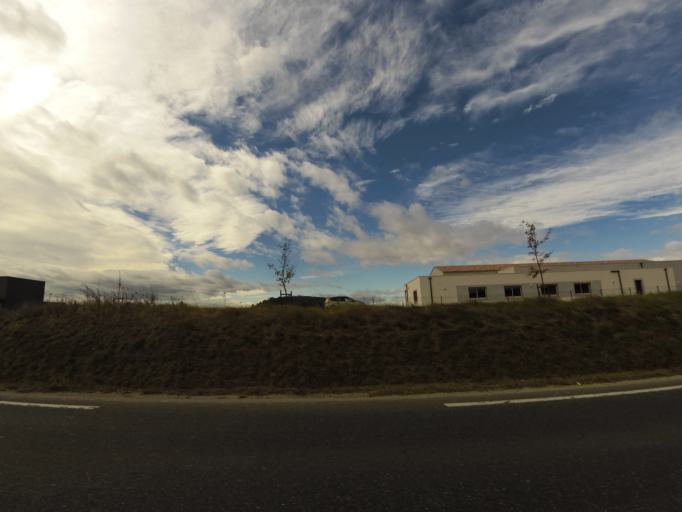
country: FR
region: Languedoc-Roussillon
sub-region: Departement du Gard
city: Calvisson
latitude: 43.7859
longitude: 4.2062
